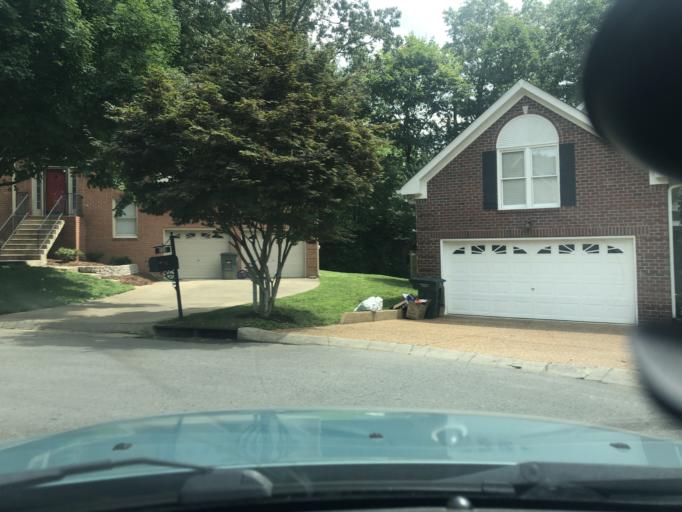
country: US
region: Tennessee
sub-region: Davidson County
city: Lakewood
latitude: 36.1312
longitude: -86.6366
